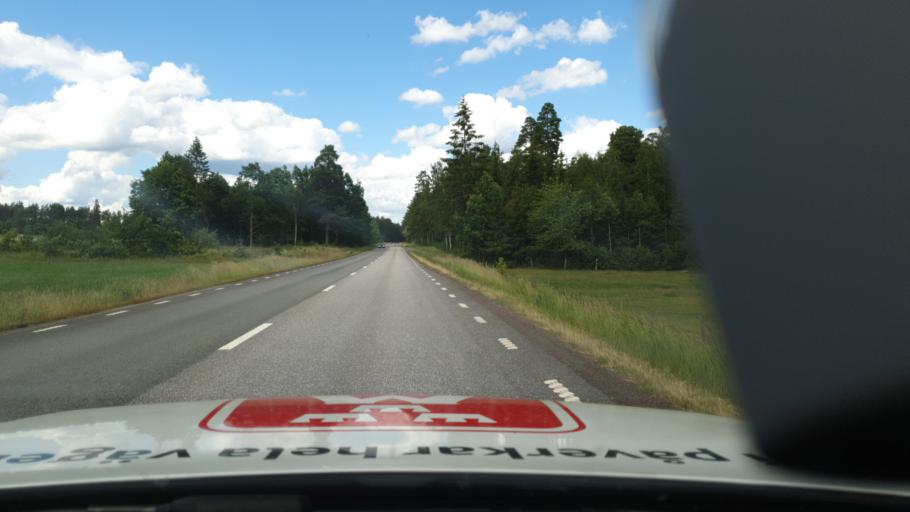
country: SE
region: Vaestra Goetaland
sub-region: Karlsborgs Kommun
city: Molltorp
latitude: 58.4585
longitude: 14.4040
